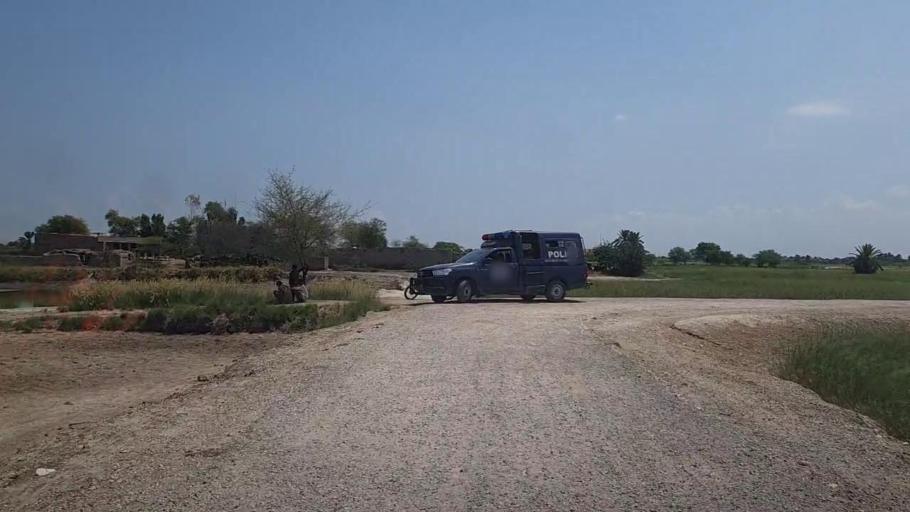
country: PK
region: Sindh
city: Ubauro
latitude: 28.1640
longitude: 69.7643
